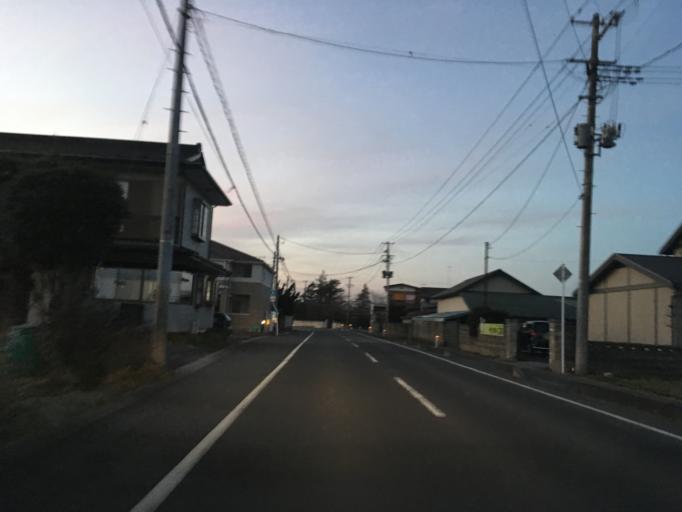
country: JP
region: Miyagi
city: Wakuya
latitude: 38.7117
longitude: 141.2345
